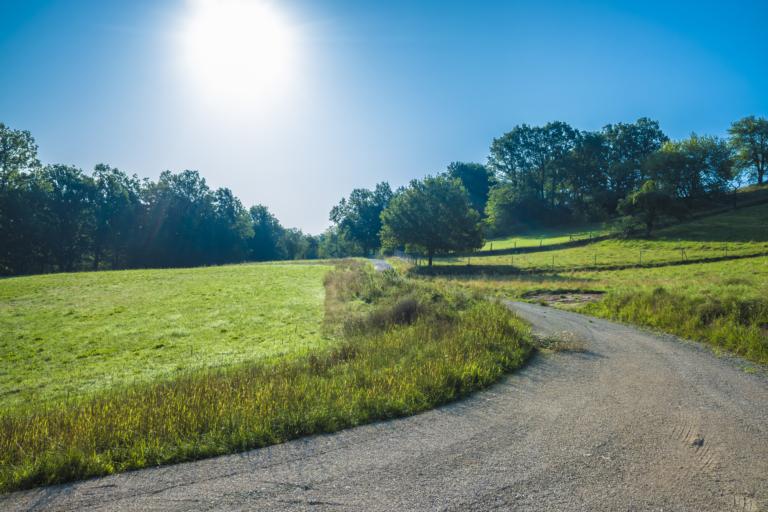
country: DE
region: Bavaria
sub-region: Upper Franconia
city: Viereth-Trunstadt
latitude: 49.9046
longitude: 10.7634
